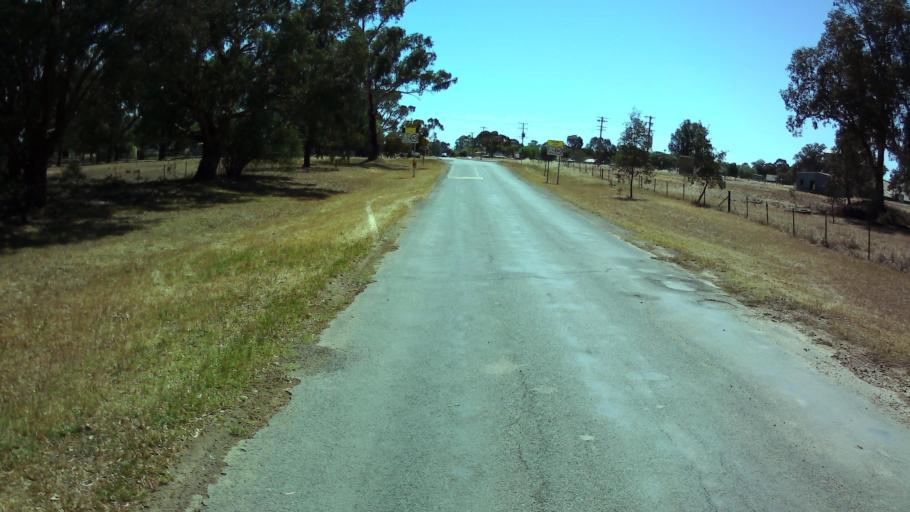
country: AU
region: New South Wales
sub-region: Weddin
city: Grenfell
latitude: -33.9989
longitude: 148.3990
